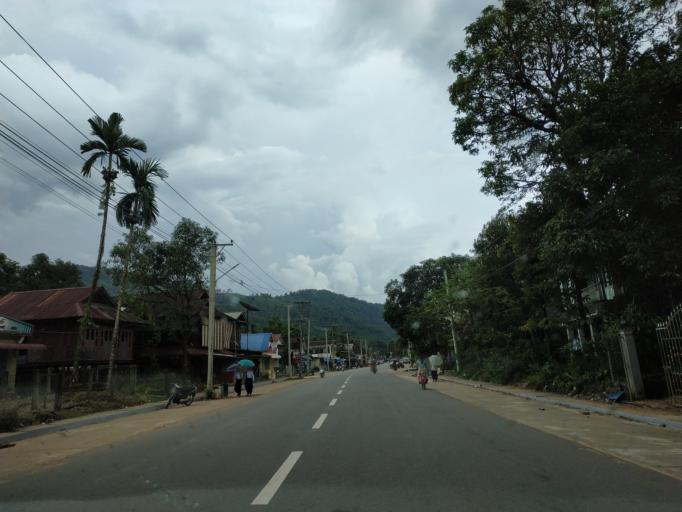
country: MM
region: Tanintharyi
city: Dawei
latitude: 13.8629
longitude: 98.2643
